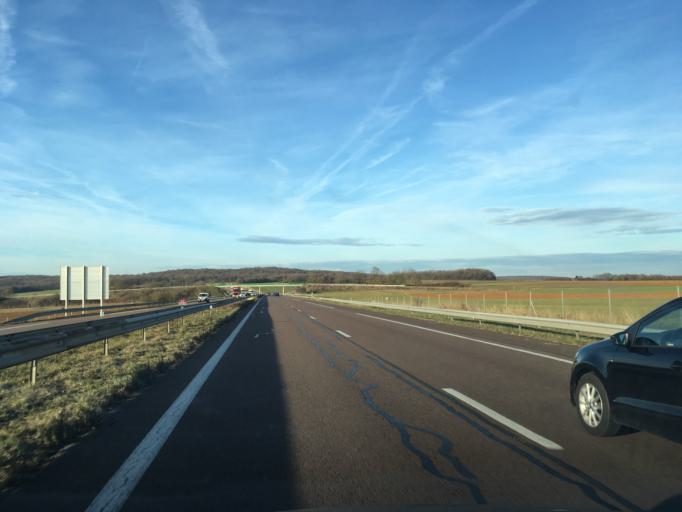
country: FR
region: Bourgogne
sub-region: Departement de l'Yonne
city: Avallon
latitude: 47.5683
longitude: 3.9396
